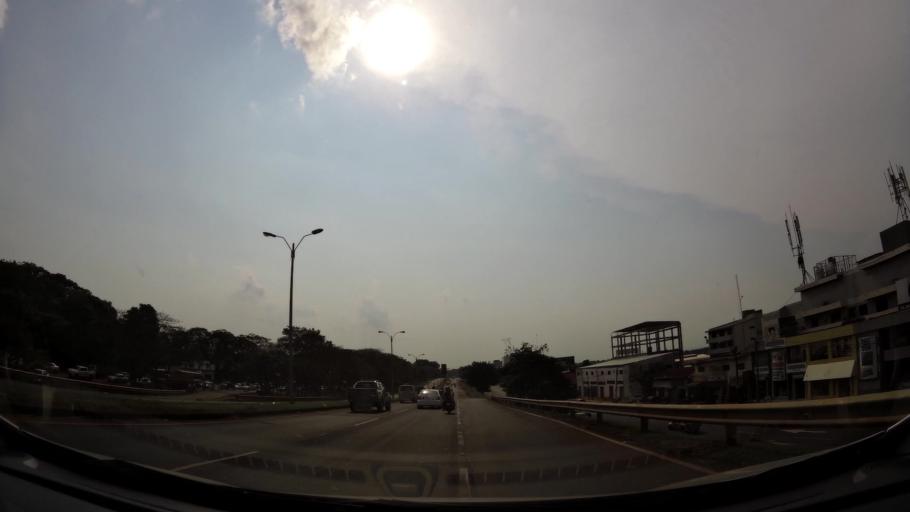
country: PY
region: Alto Parana
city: Ciudad del Este
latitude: -25.5063
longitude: -54.6410
